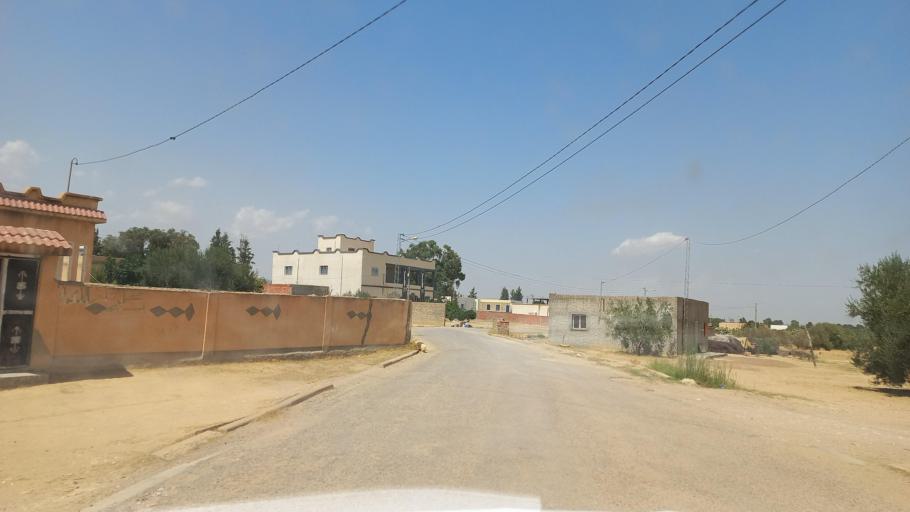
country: TN
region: Al Qasrayn
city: Kasserine
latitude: 35.2490
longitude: 9.0276
